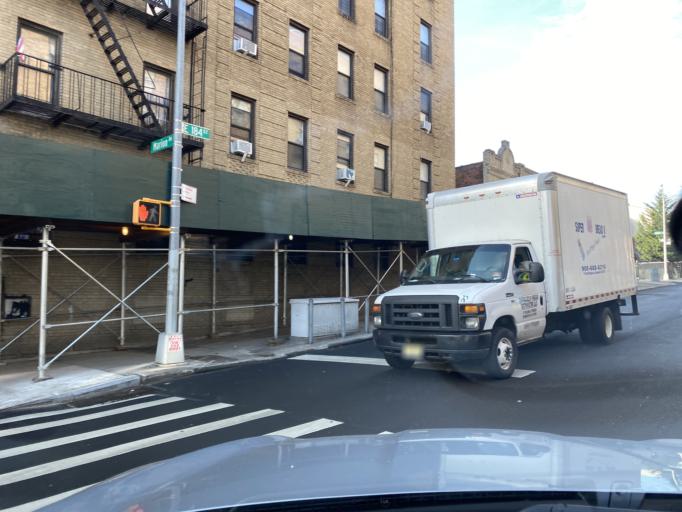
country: US
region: New York
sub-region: Bronx
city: The Bronx
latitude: 40.8582
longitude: -73.8957
